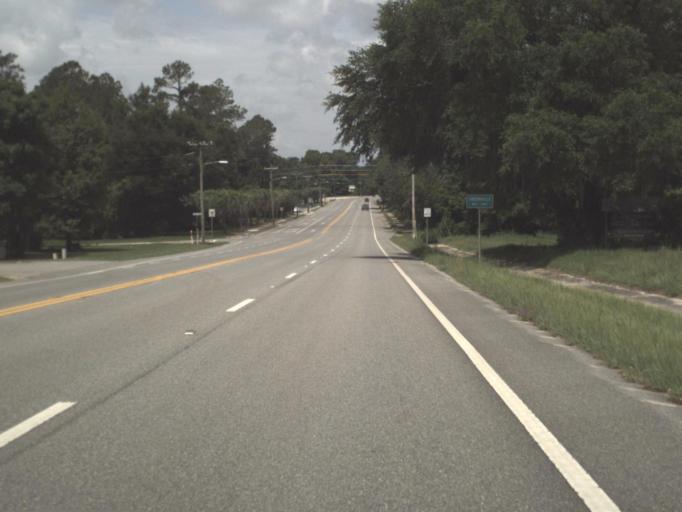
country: US
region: Florida
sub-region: Madison County
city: Madison
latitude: 30.4695
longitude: -83.6236
